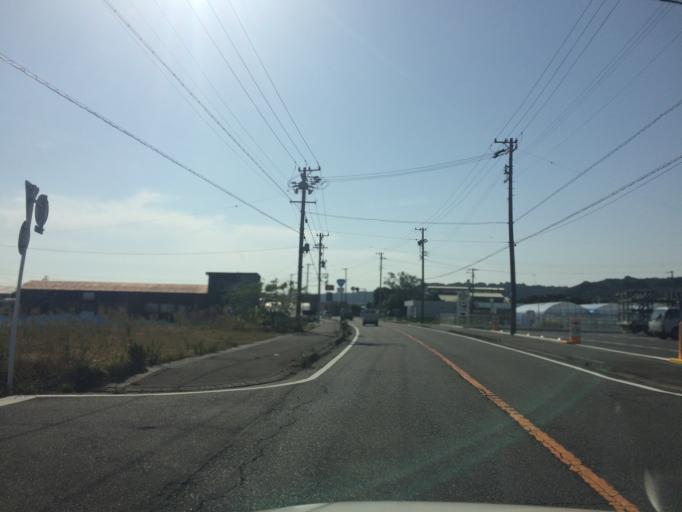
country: JP
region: Shizuoka
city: Sagara
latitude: 34.7262
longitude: 138.2205
